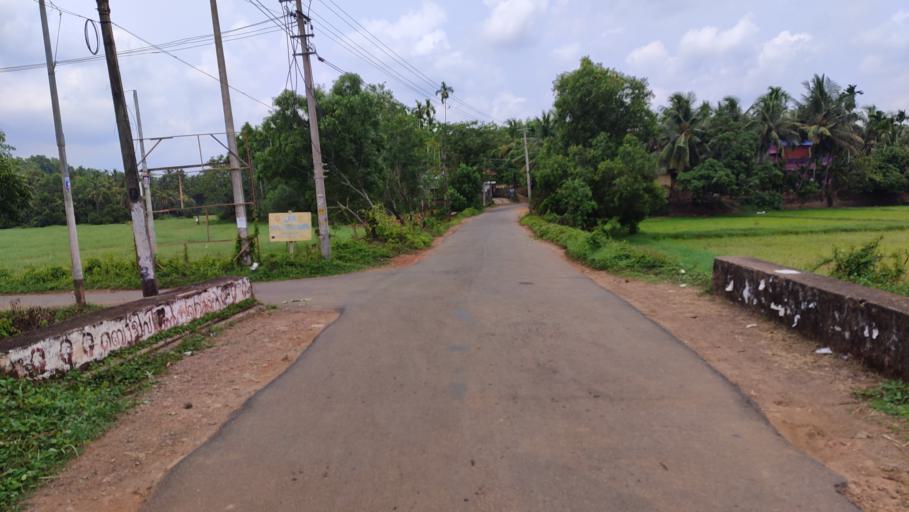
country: IN
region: Kerala
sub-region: Kasaragod District
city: Kannangad
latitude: 12.3206
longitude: 75.1124
